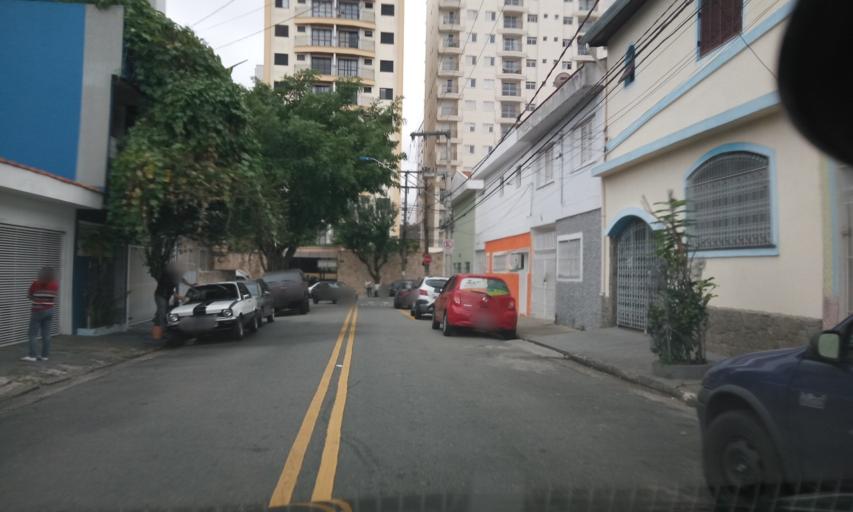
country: BR
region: Sao Paulo
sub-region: Sao Caetano Do Sul
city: Sao Caetano do Sul
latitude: -23.6225
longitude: -46.5726
